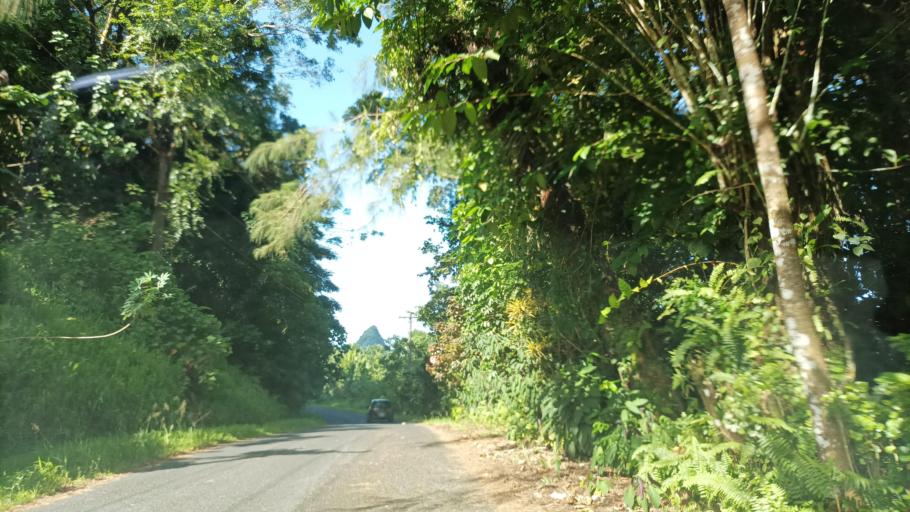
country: FM
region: Pohnpei
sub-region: Madolenihm Municipality
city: Madolenihm Municipality Government
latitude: 6.8600
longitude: 158.2928
